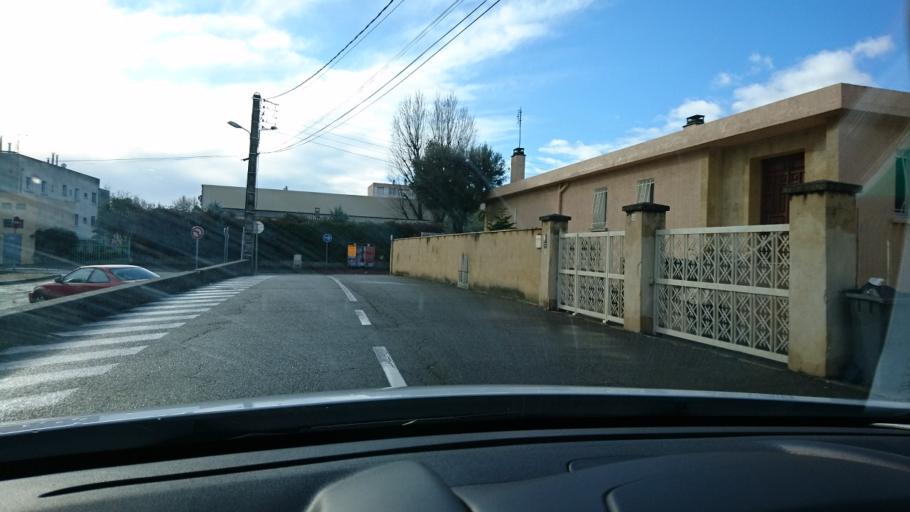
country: FR
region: Languedoc-Roussillon
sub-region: Departement du Gard
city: Pont-Saint-Esprit
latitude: 44.2570
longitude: 4.6446
